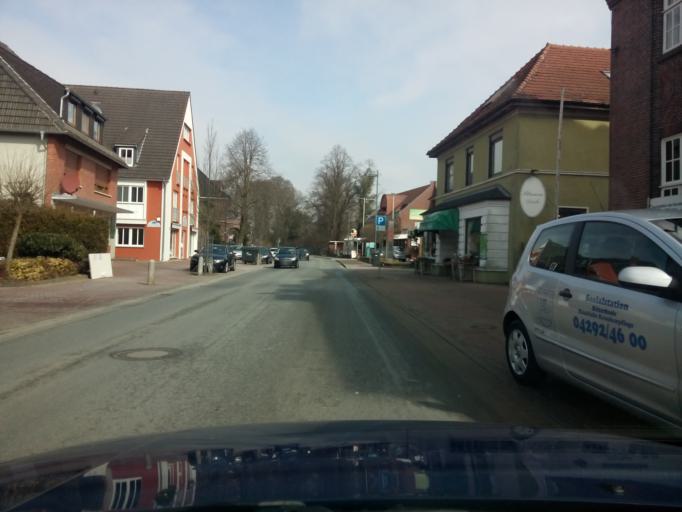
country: DE
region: Lower Saxony
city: Ritterhude
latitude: 53.1810
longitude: 8.7555
